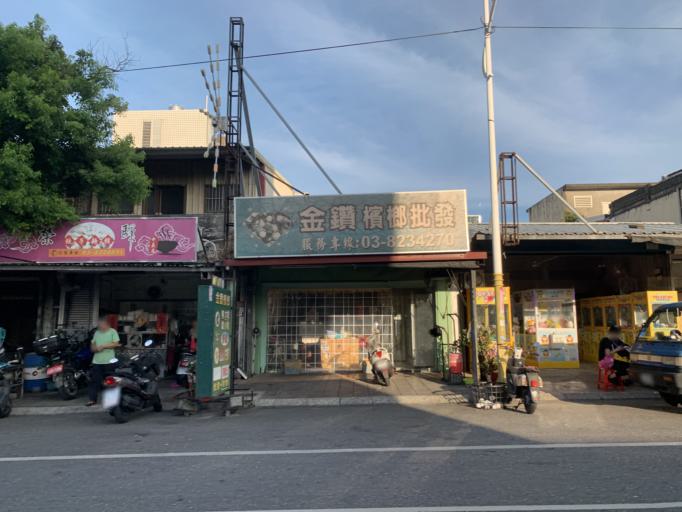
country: TW
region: Taiwan
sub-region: Hualien
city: Hualian
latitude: 23.9958
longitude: 121.6296
